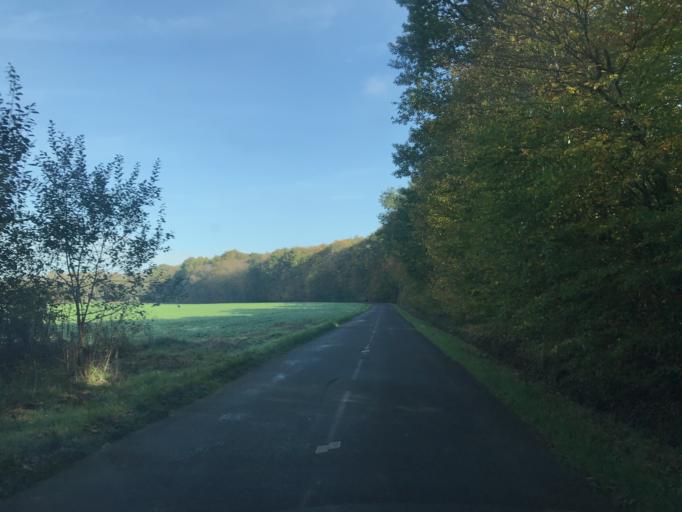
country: FR
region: Haute-Normandie
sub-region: Departement de l'Eure
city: Saint-Just
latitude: 49.0866
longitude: 1.4154
